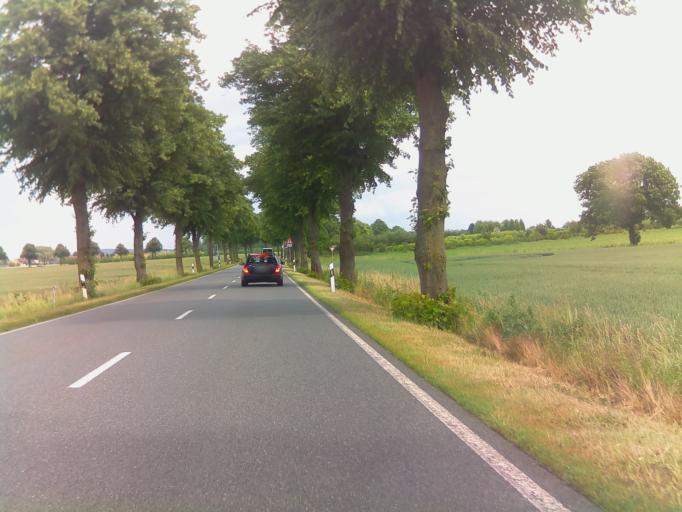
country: DE
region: Lower Saxony
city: Springe
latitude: 52.1750
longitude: 9.6298
